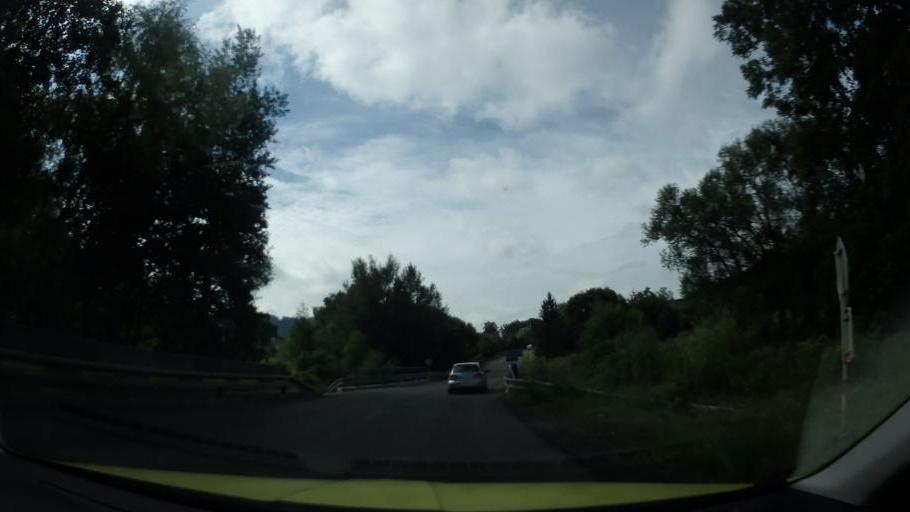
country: CZ
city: Hodslavice
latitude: 49.5288
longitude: 18.0178
